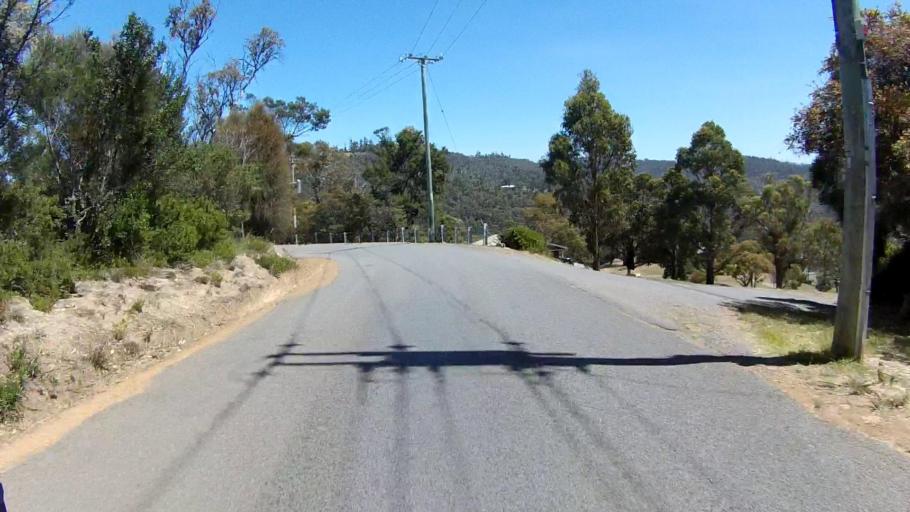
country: AU
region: Tasmania
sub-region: Clarence
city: Cambridge
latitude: -42.8538
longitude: 147.4241
